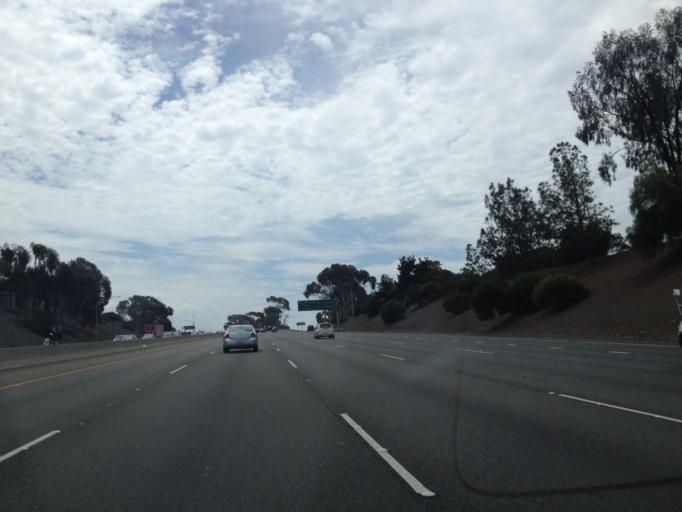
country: US
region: California
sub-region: Orange County
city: San Clemente
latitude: 33.4351
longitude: -117.6176
